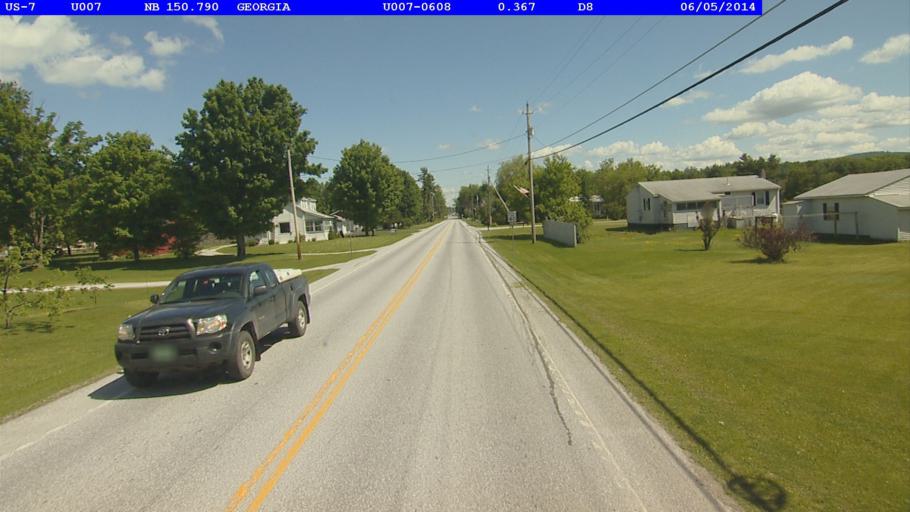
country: US
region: Vermont
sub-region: Chittenden County
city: Milton
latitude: 44.6845
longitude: -73.1109
